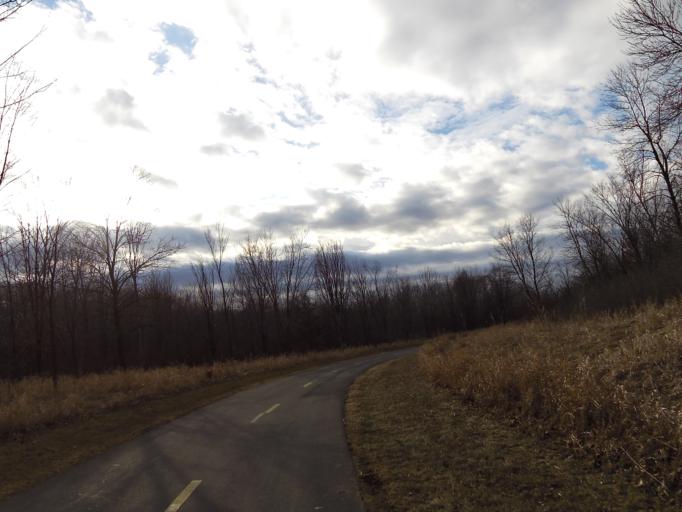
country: US
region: Minnesota
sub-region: Scott County
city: Prior Lake
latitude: 44.6950
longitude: -93.3858
